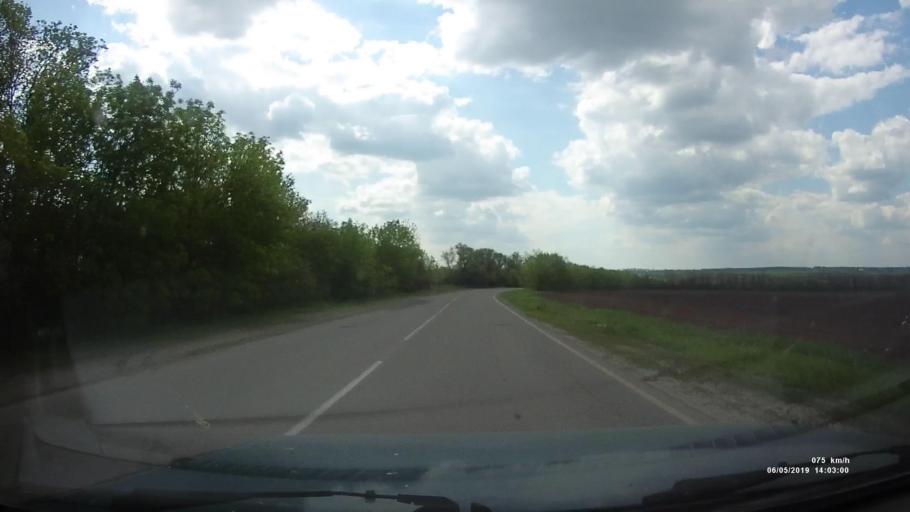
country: RU
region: Rostov
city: Shakhty
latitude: 47.6809
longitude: 40.3537
